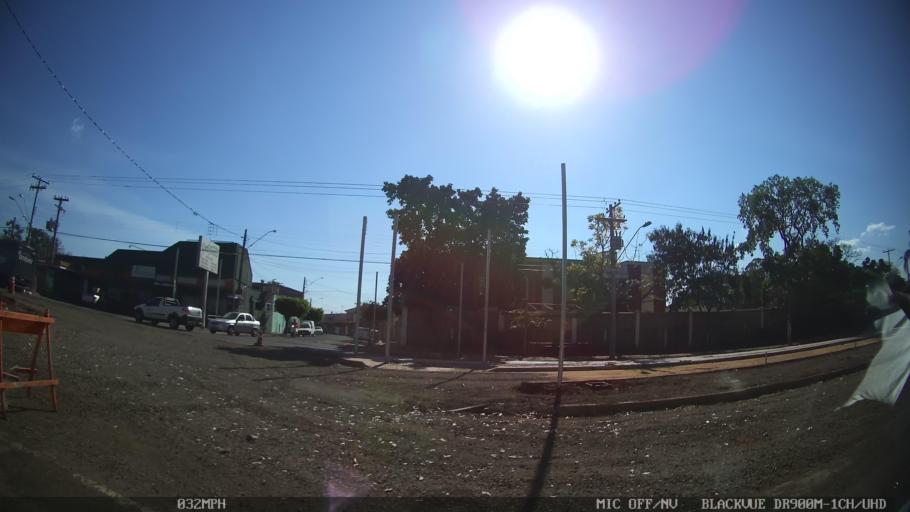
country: BR
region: Sao Paulo
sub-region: Ribeirao Preto
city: Ribeirao Preto
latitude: -21.1548
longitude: -47.7827
